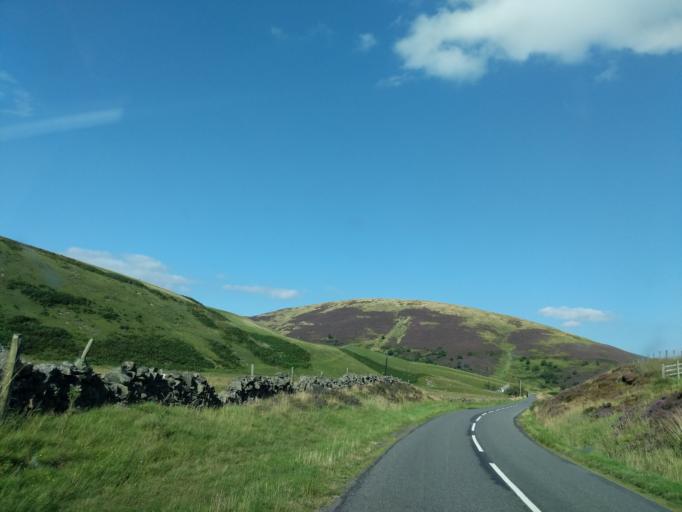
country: GB
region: Scotland
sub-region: Midlothian
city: Gorebridge
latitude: 55.7398
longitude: -3.0339
